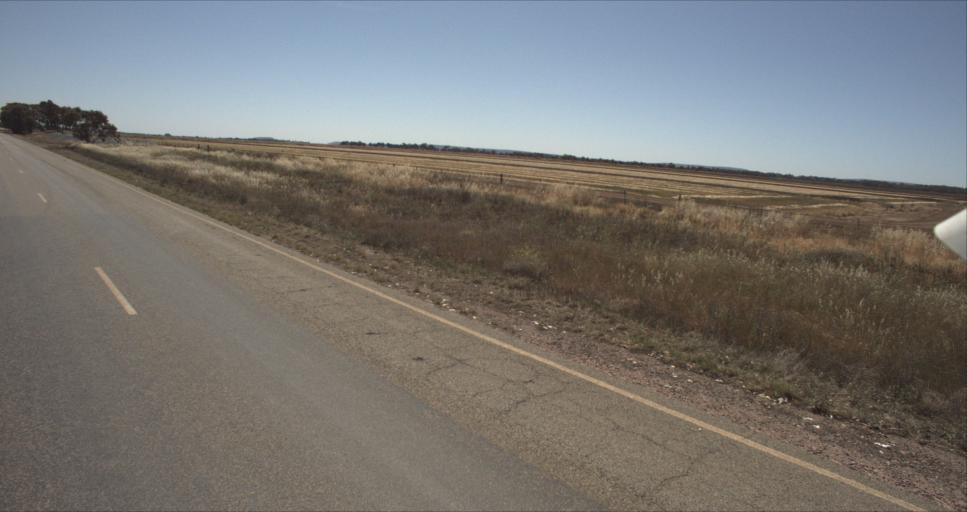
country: AU
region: New South Wales
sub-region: Leeton
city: Leeton
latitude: -34.4966
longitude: 146.2877
